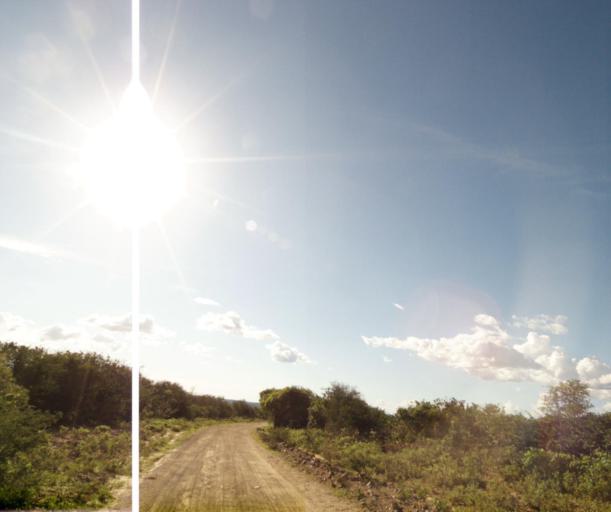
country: BR
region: Bahia
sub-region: Tanhacu
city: Tanhacu
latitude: -14.1895
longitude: -40.9731
